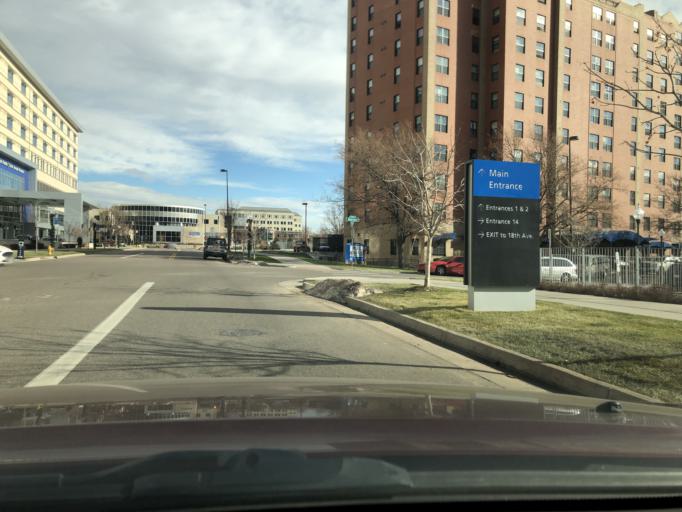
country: US
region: Colorado
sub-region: Denver County
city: Denver
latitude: 39.7458
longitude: -104.9725
